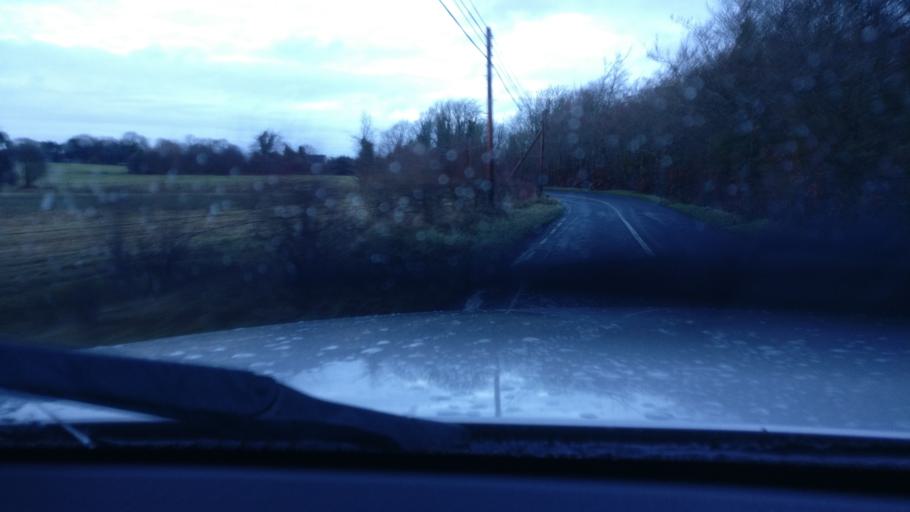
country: IE
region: Connaught
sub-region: County Galway
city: Ballinasloe
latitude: 53.2793
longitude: -8.2417
